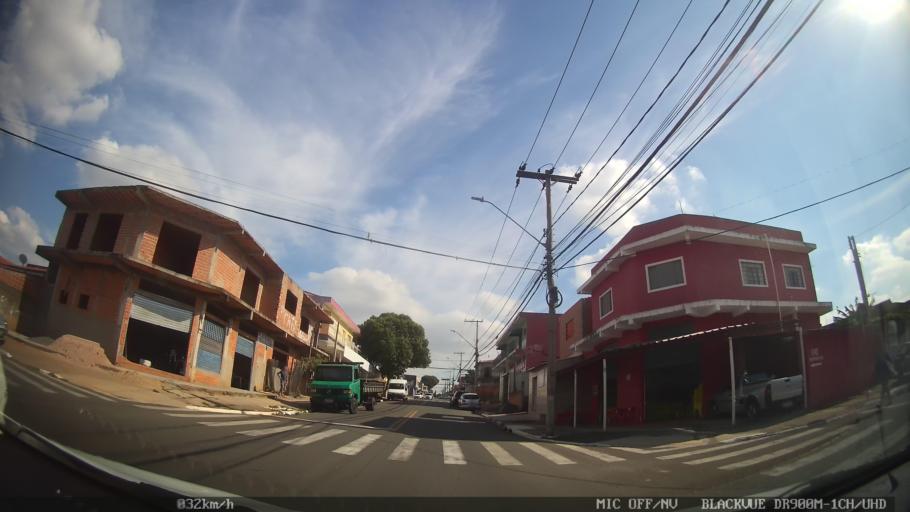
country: BR
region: Sao Paulo
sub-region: Hortolandia
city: Hortolandia
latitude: -22.9018
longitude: -47.2469
